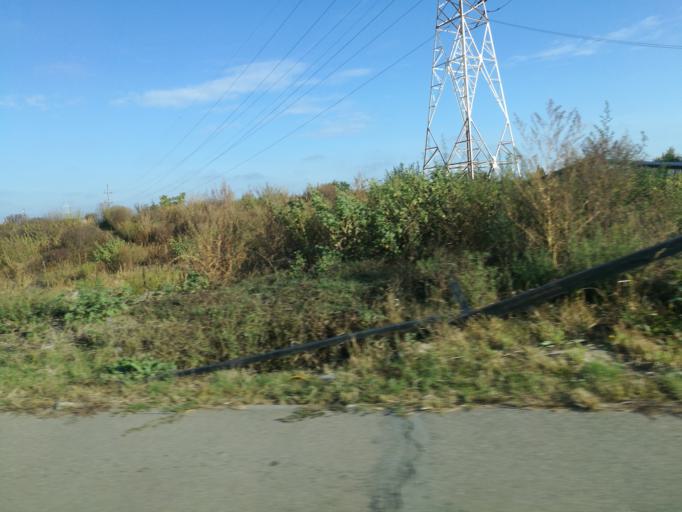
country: RO
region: Bihor
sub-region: Comuna Biharea
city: Oradea
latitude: 47.0402
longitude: 21.9299
